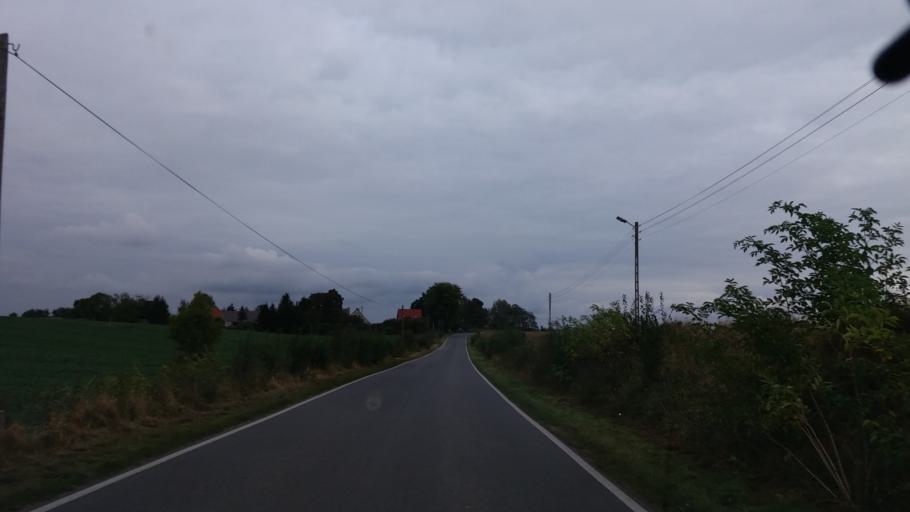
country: PL
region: West Pomeranian Voivodeship
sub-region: Powiat choszczenski
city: Pelczyce
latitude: 53.0342
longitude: 15.3418
